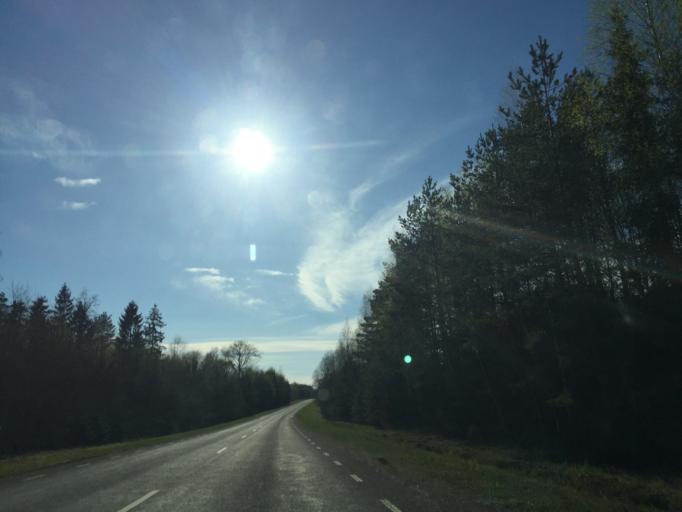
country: EE
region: Valgamaa
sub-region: Valga linn
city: Valga
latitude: 57.7556
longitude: 26.1717
